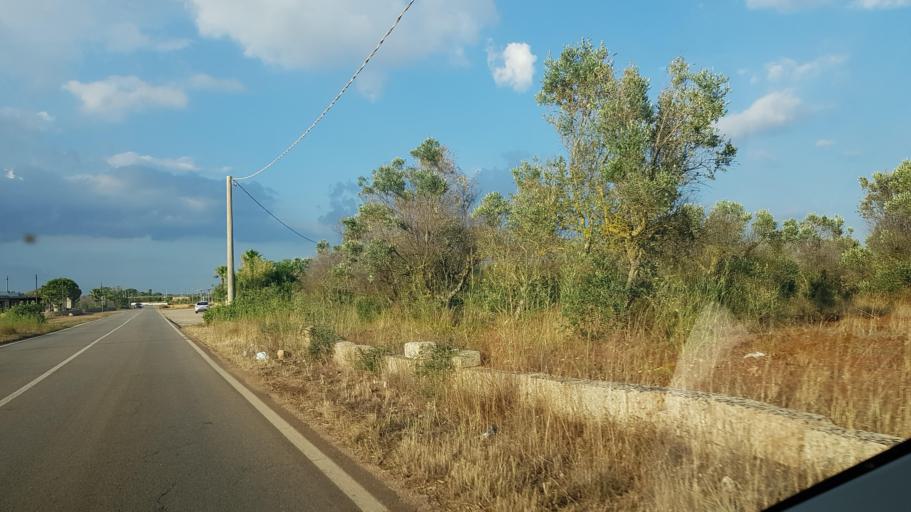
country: IT
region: Apulia
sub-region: Provincia di Lecce
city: Acquarica del Capo
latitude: 39.8712
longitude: 18.2216
